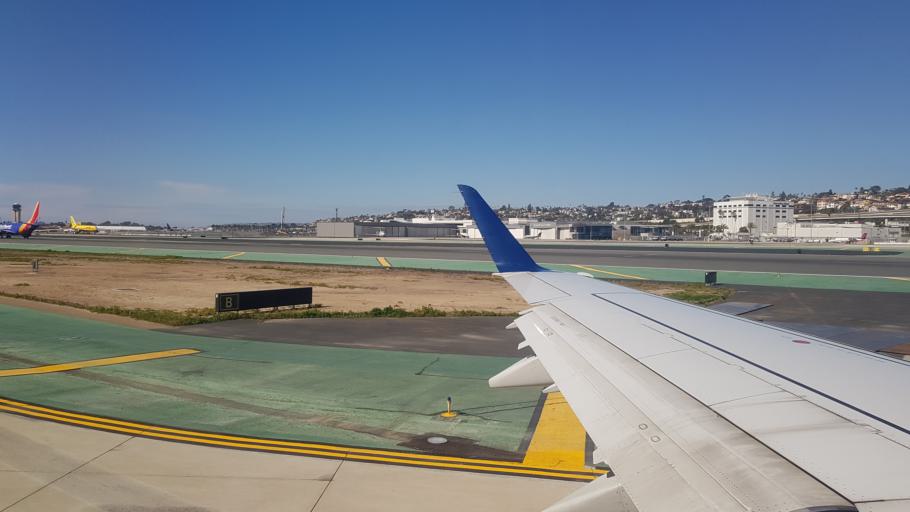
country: US
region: California
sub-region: San Diego County
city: San Diego
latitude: 32.7296
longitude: -117.1774
